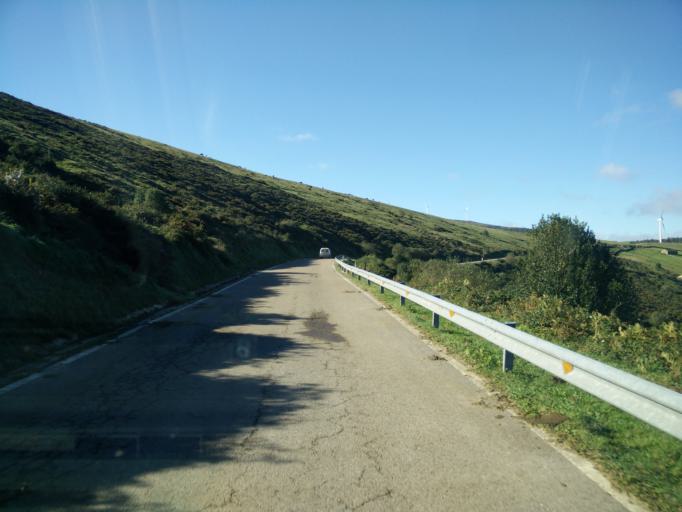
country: ES
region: Cantabria
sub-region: Provincia de Cantabria
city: San Pedro del Romeral
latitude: 43.0853
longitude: -3.8210
